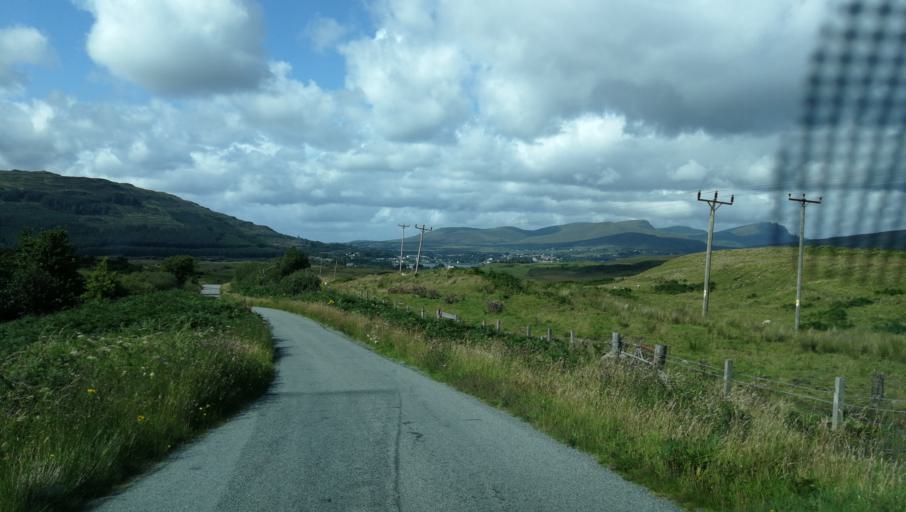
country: GB
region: Scotland
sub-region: Highland
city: Portree
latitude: 57.3800
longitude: -6.1708
